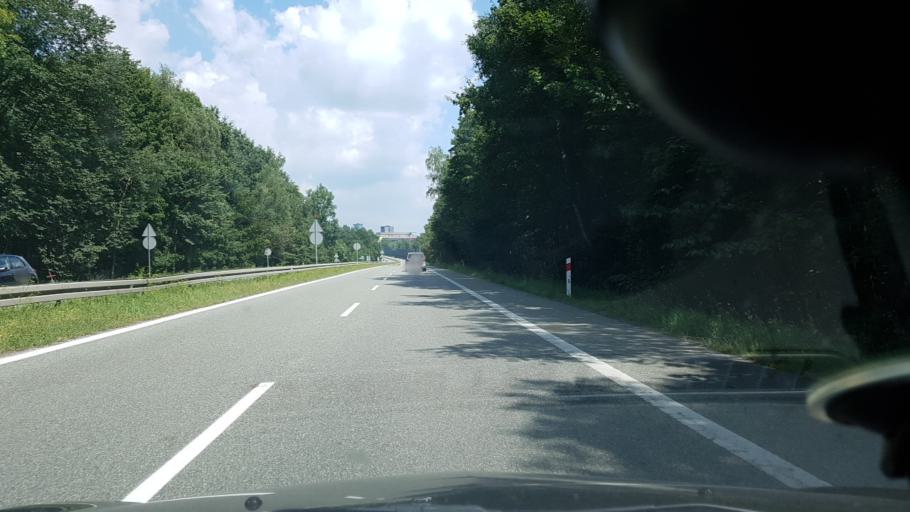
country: PL
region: Silesian Voivodeship
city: Gardawice
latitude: 50.1272
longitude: 18.8226
